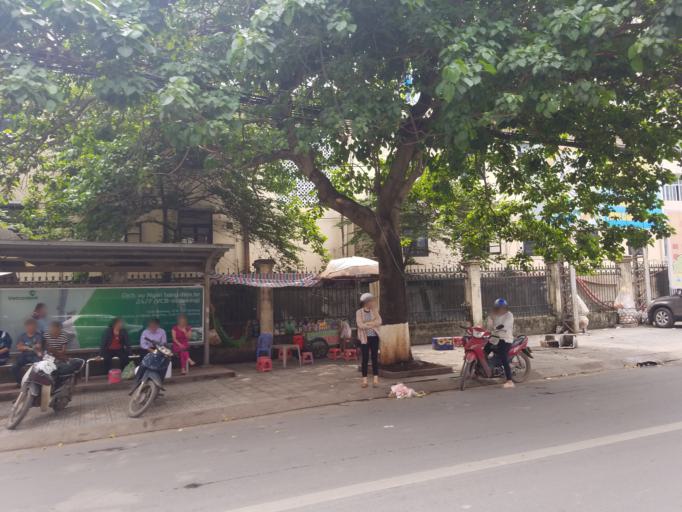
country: VN
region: Thai Nguyen
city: Thanh Pho Thai Nguyen
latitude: 21.5892
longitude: 105.8276
